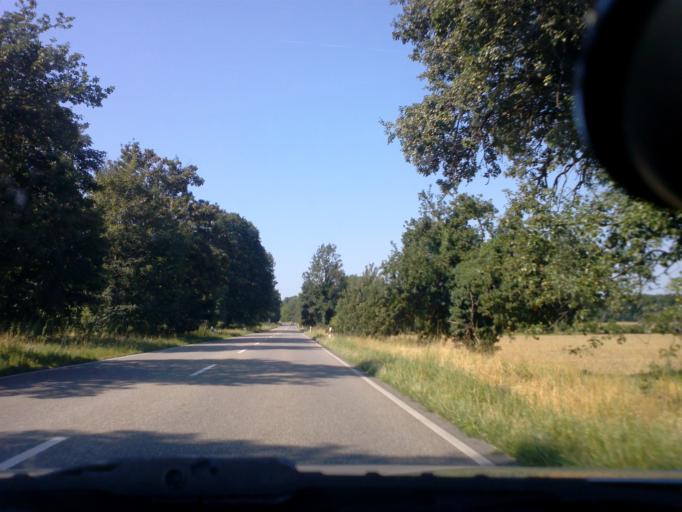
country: DE
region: Baden-Wuerttemberg
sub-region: Karlsruhe Region
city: Weingarten
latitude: 49.0260
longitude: 8.5096
